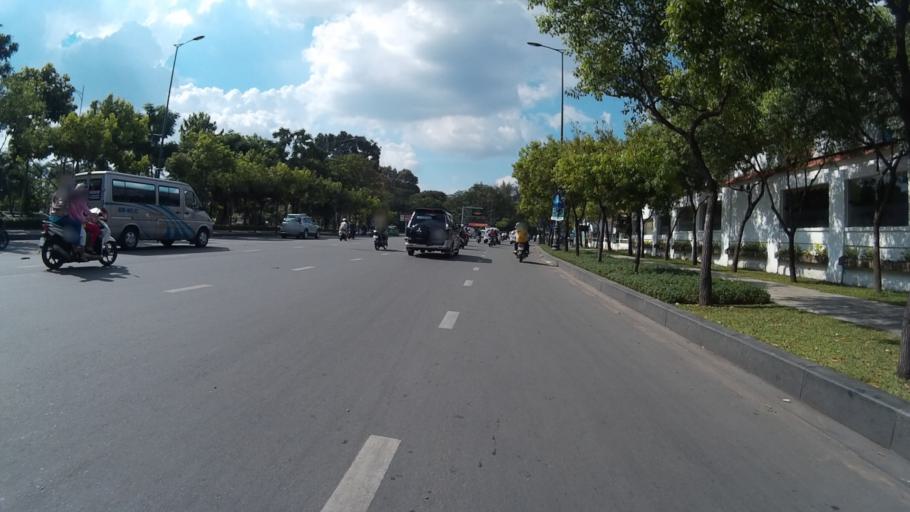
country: VN
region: Ho Chi Minh City
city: Quan Phu Nhuan
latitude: 10.8009
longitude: 106.6667
